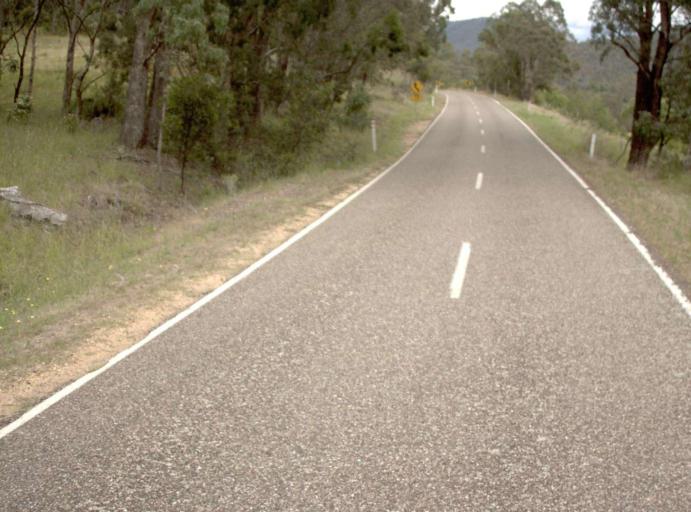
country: AU
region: Victoria
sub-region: East Gippsland
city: Bairnsdale
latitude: -37.5307
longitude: 147.2208
